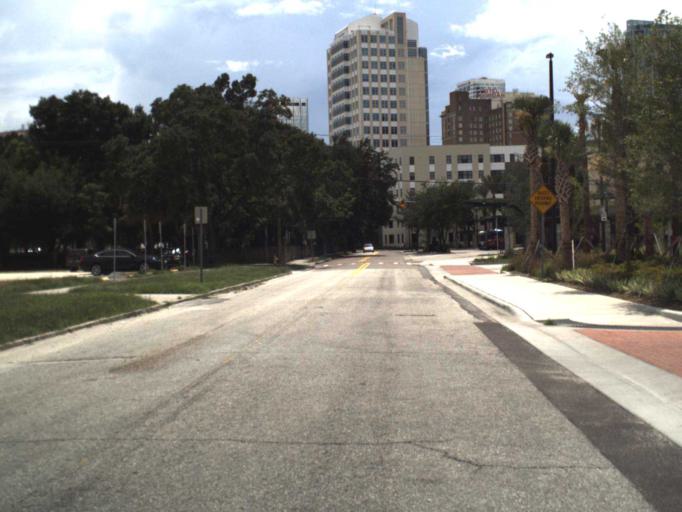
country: US
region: Florida
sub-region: Hillsborough County
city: Tampa
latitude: 27.9562
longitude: -82.4581
